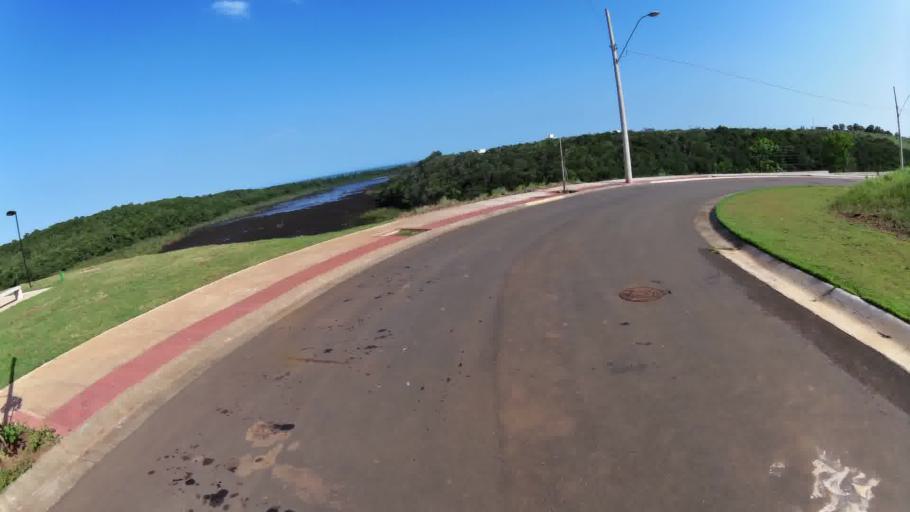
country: BR
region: Espirito Santo
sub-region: Guarapari
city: Guarapari
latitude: -20.7137
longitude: -40.5287
